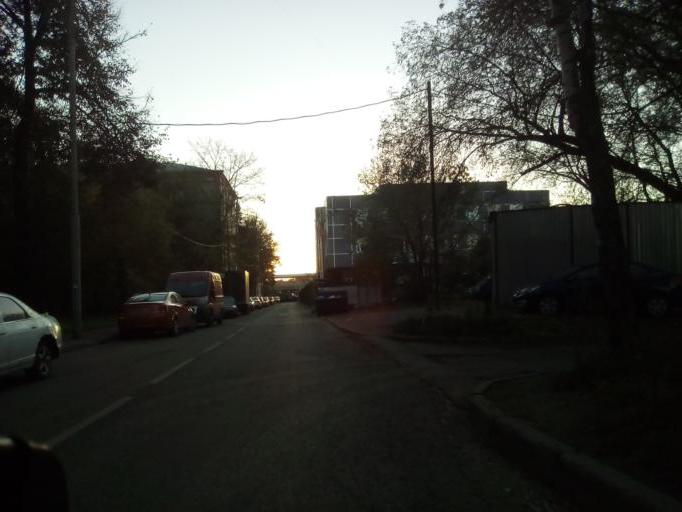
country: RU
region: Moskovskaya
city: Koptevo
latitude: 55.8144
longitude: 37.4903
